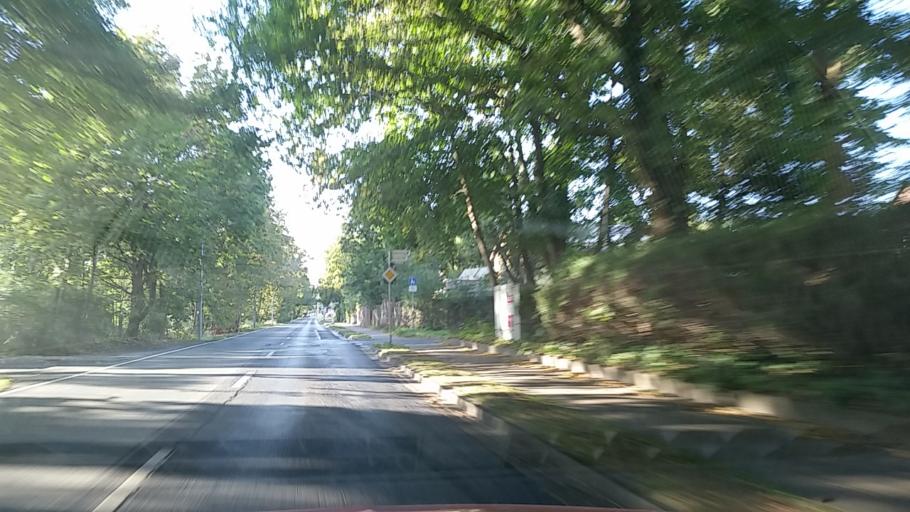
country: DE
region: Lower Saxony
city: Braunschweig
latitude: 52.3009
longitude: 10.5498
